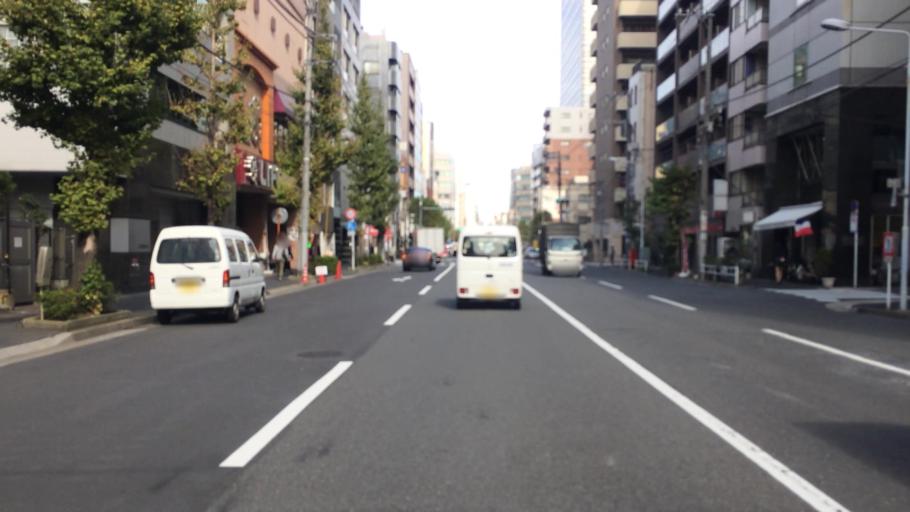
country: JP
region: Tokyo
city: Tokyo
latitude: 35.6993
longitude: 139.7805
